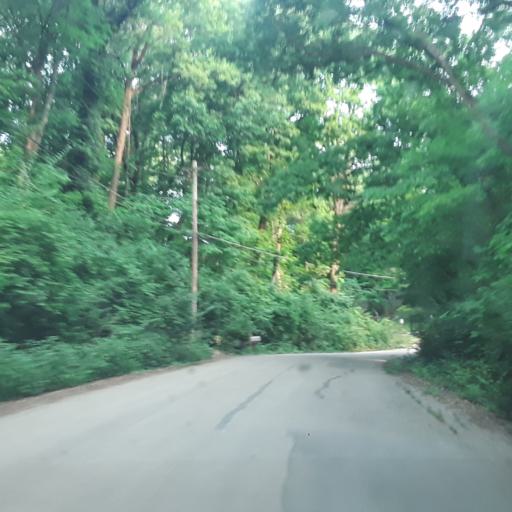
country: US
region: Tennessee
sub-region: Williamson County
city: Brentwood
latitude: 36.0582
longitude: -86.7822
